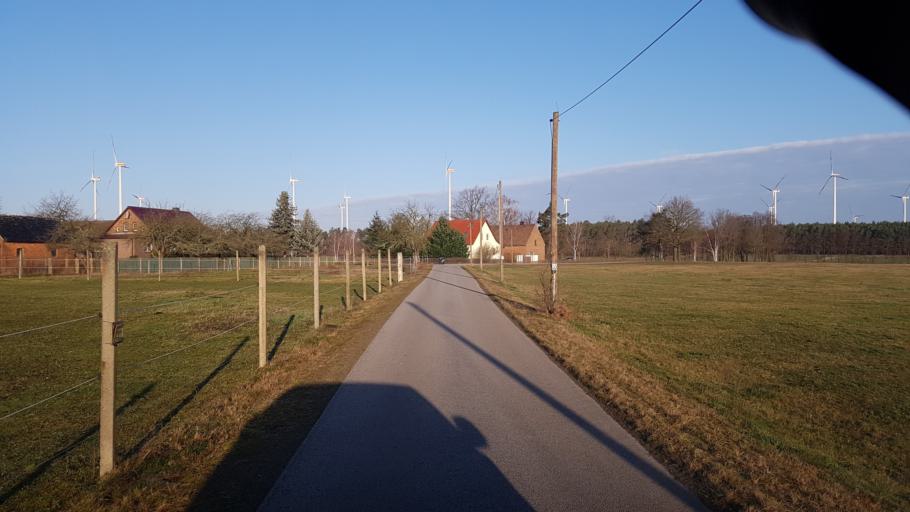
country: DE
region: Brandenburg
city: Calau
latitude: 51.7297
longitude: 13.9008
